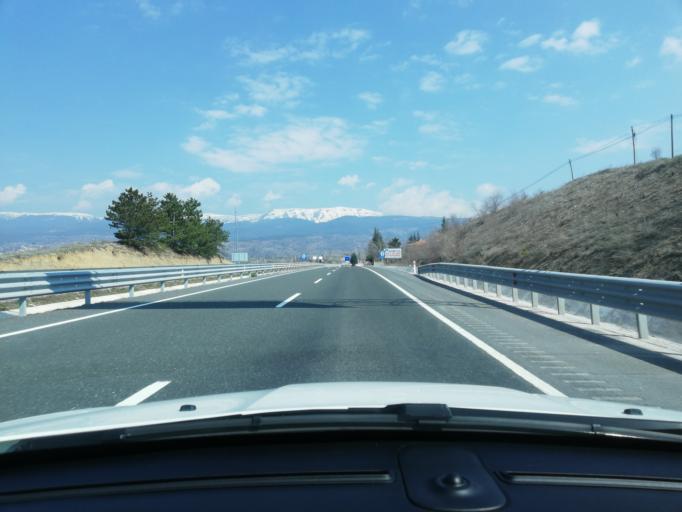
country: TR
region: Cankiri
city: Ilgaz
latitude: 40.9208
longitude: 33.6489
